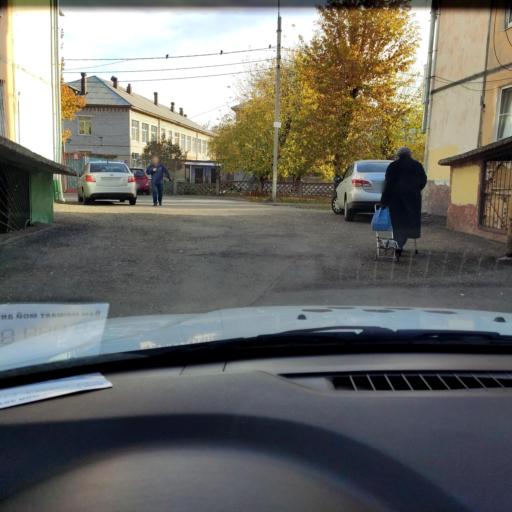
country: RU
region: Samara
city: Tol'yatti
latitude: 53.5126
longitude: 49.4192
